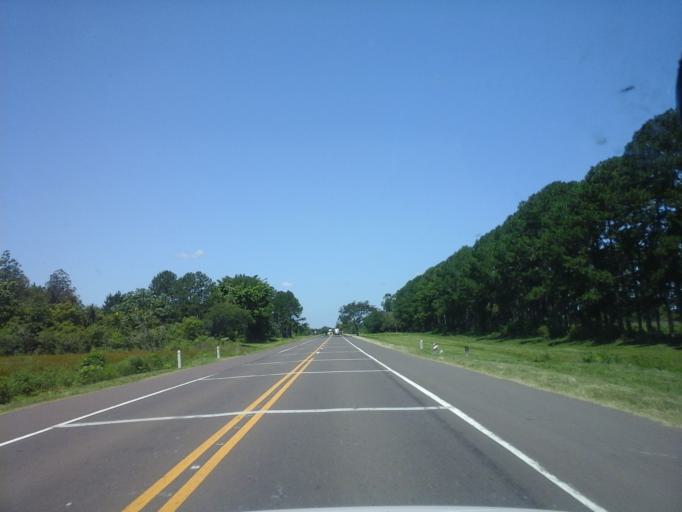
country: AR
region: Corrientes
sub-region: Departamento de San Cosme
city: San Cosme
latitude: -27.3723
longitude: -58.4840
